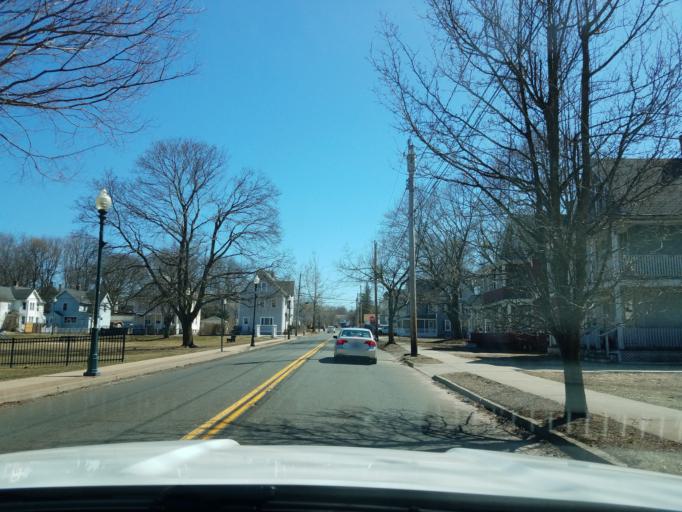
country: US
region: Connecticut
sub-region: New Haven County
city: Wallingford
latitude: 41.4561
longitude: -72.8327
